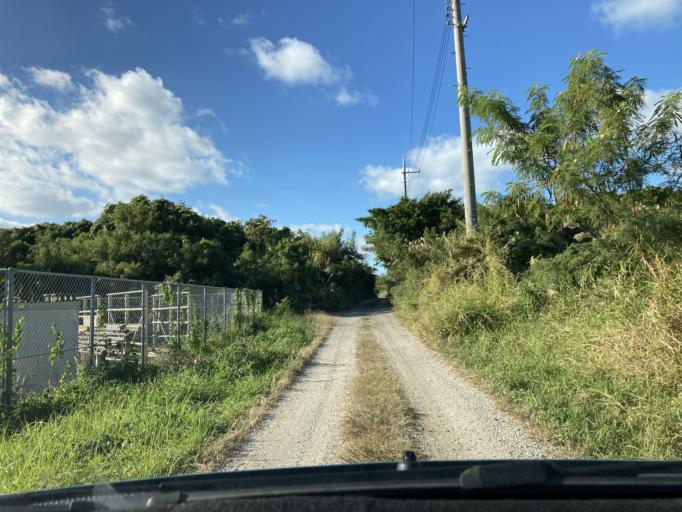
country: JP
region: Okinawa
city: Katsuren-haebaru
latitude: 26.3187
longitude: 127.9254
